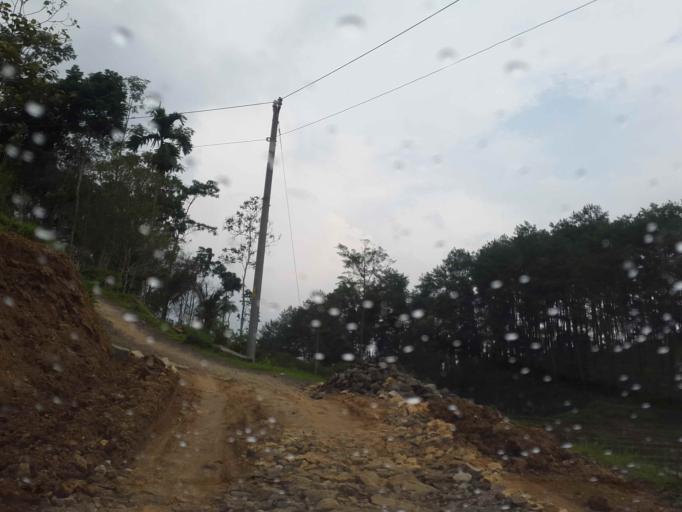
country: ID
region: Central Java
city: Bantarmangu
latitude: -7.3432
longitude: 108.9427
